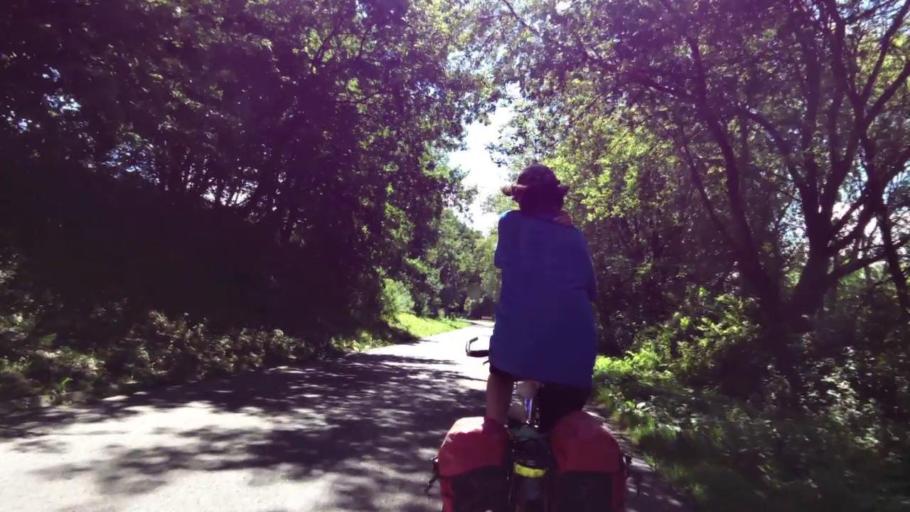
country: PL
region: West Pomeranian Voivodeship
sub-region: Koszalin
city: Koszalin
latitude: 54.2848
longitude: 16.2095
